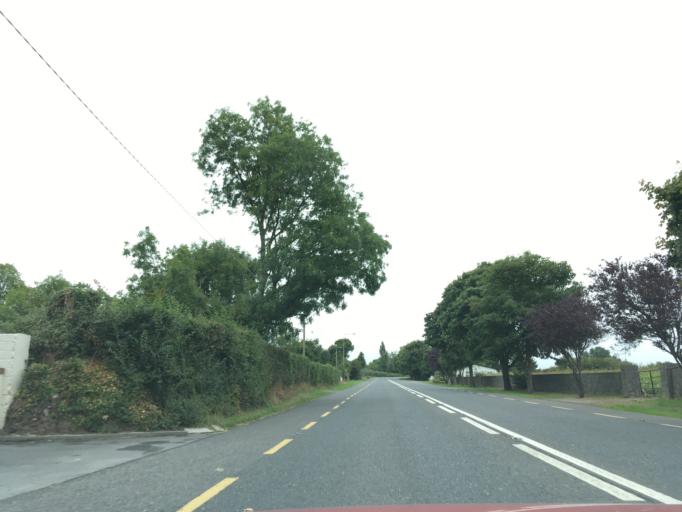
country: IE
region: Munster
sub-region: South Tipperary
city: Cluain Meala
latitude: 52.3620
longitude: -7.5710
